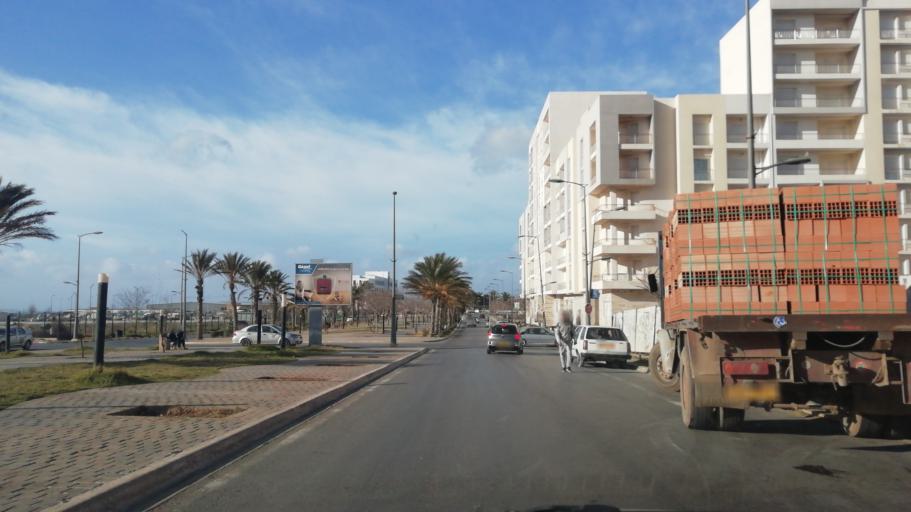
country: DZ
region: Oran
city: Bir el Djir
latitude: 35.7234
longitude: -0.5927
